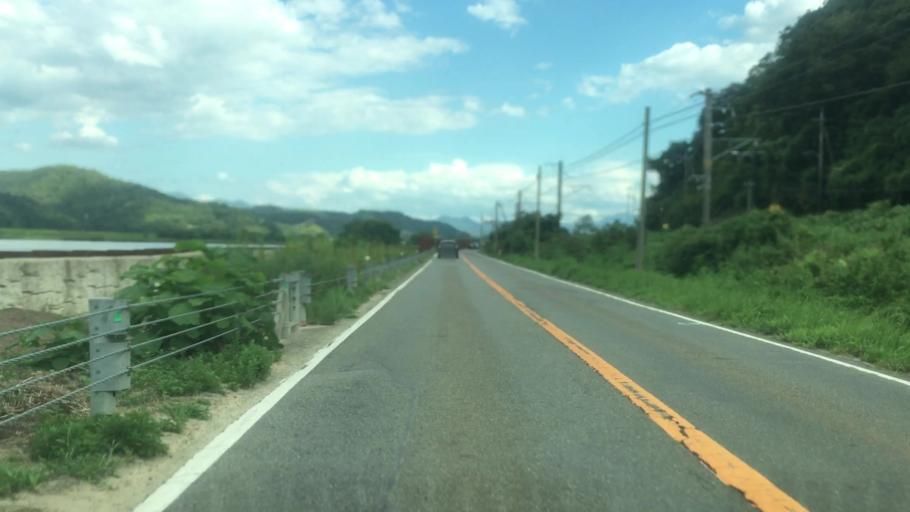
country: JP
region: Hyogo
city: Toyooka
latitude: 35.5768
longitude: 134.8033
